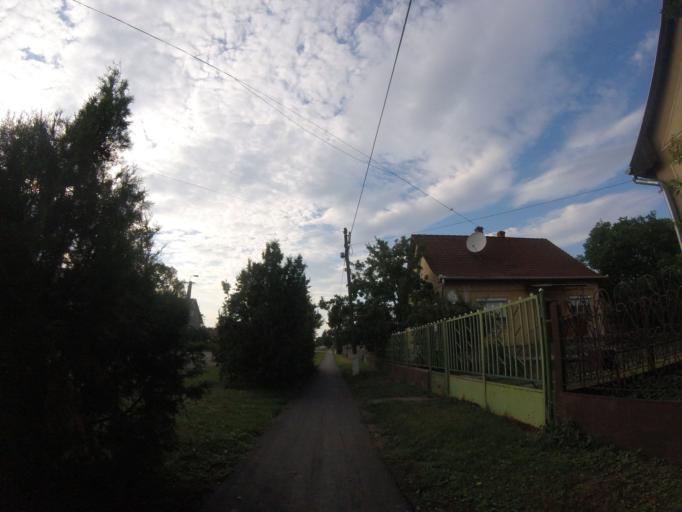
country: HU
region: Heves
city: Tiszanana
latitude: 47.6008
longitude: 20.5860
